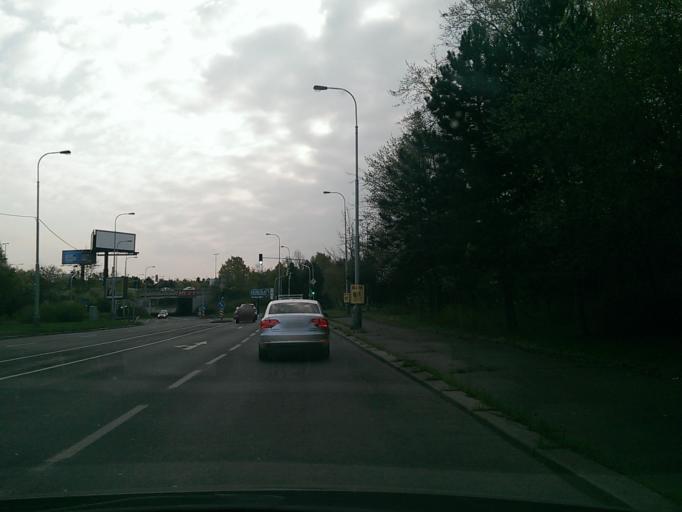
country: CZ
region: Praha
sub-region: Praha 8
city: Karlin
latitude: 50.0390
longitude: 14.4804
